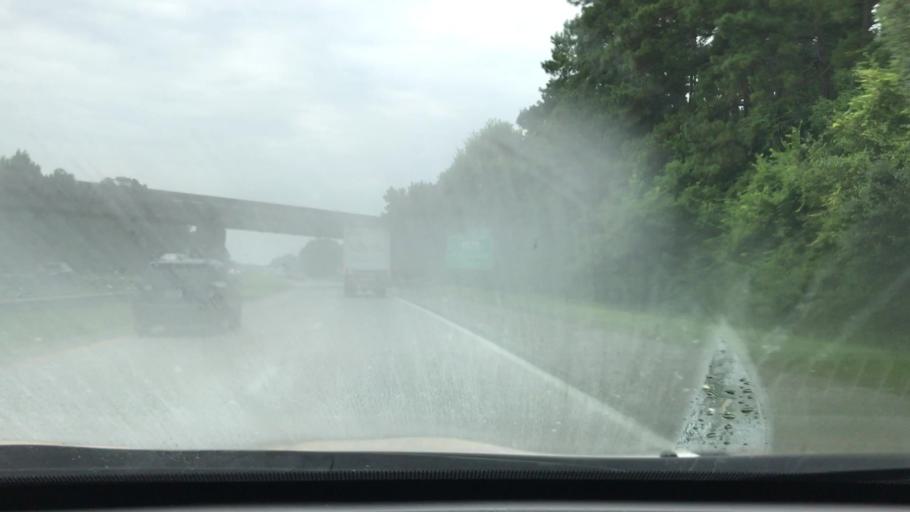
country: US
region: South Carolina
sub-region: Jasper County
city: Ridgeland
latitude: 32.5017
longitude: -80.9718
